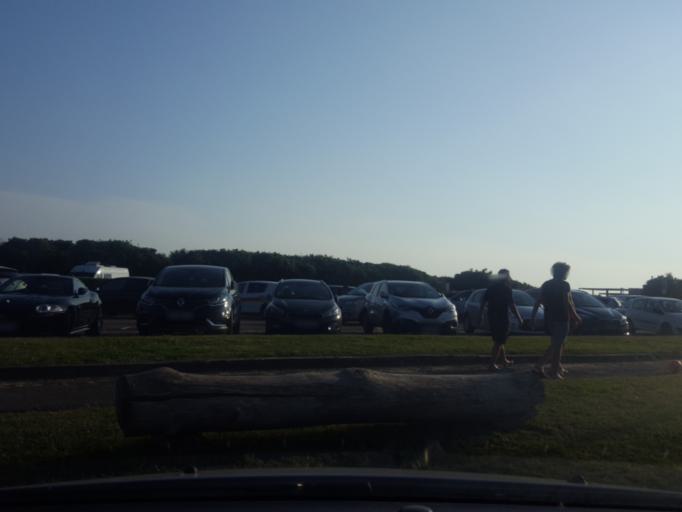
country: FR
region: Aquitaine
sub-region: Departement des Landes
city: Tarnos
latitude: 43.5769
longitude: -1.4861
